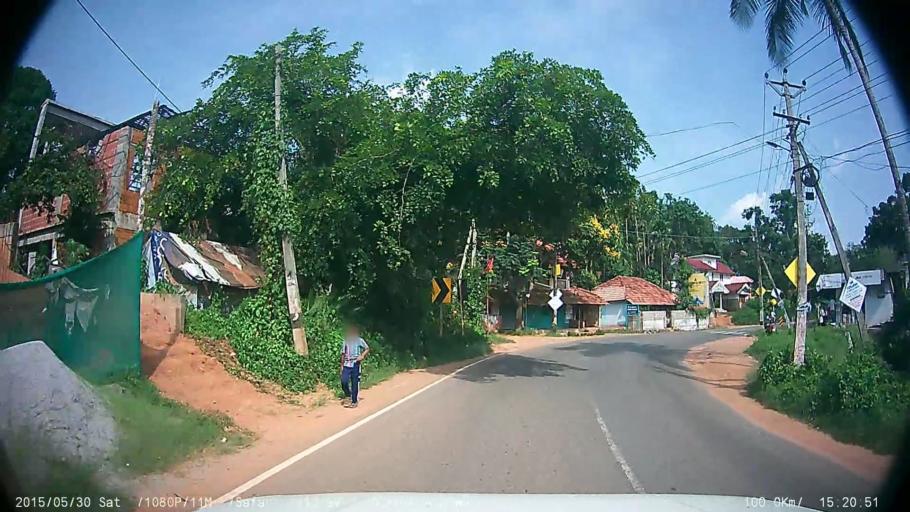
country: IN
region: Kerala
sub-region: Wayanad
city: Panamaram
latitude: 11.7519
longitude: 76.0675
